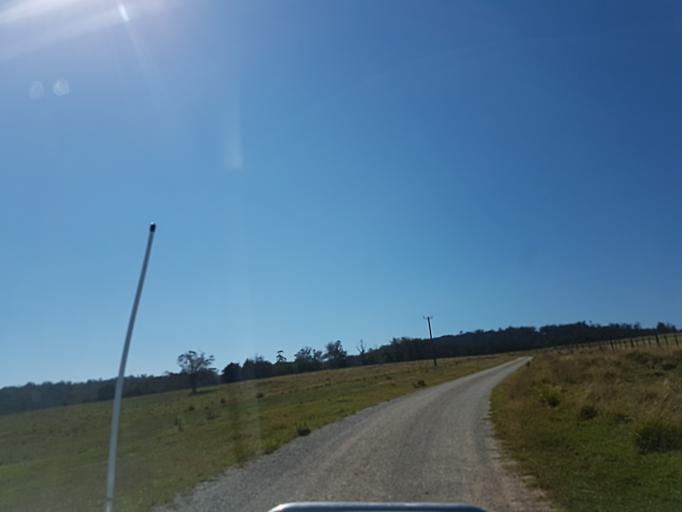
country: AU
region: Victoria
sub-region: East Gippsland
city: Lakes Entrance
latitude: -37.2314
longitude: 148.2706
